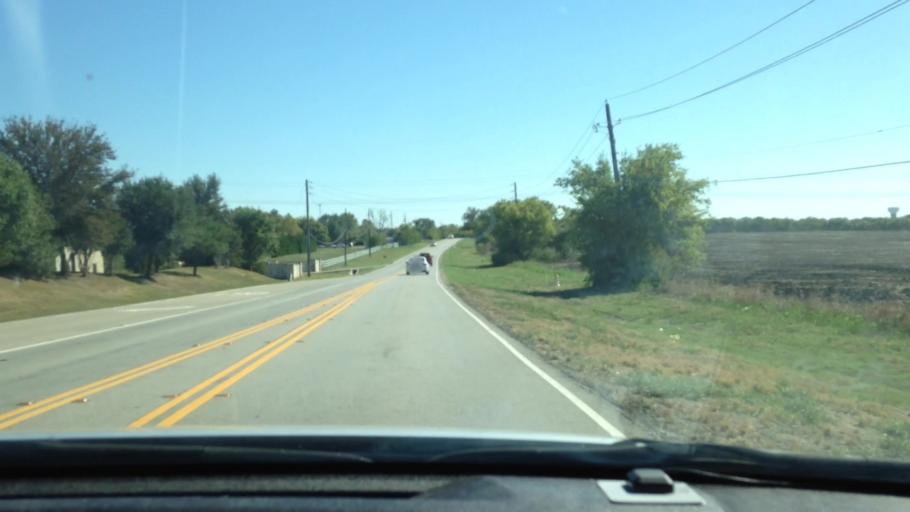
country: US
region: Texas
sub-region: Collin County
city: Lucas
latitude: 33.0661
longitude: -96.5702
